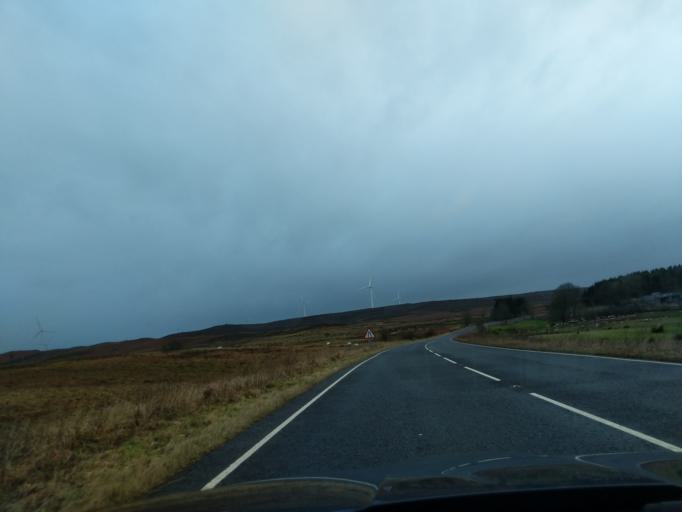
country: GB
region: England
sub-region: Northumberland
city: Rothley
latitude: 55.1759
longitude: -2.0319
